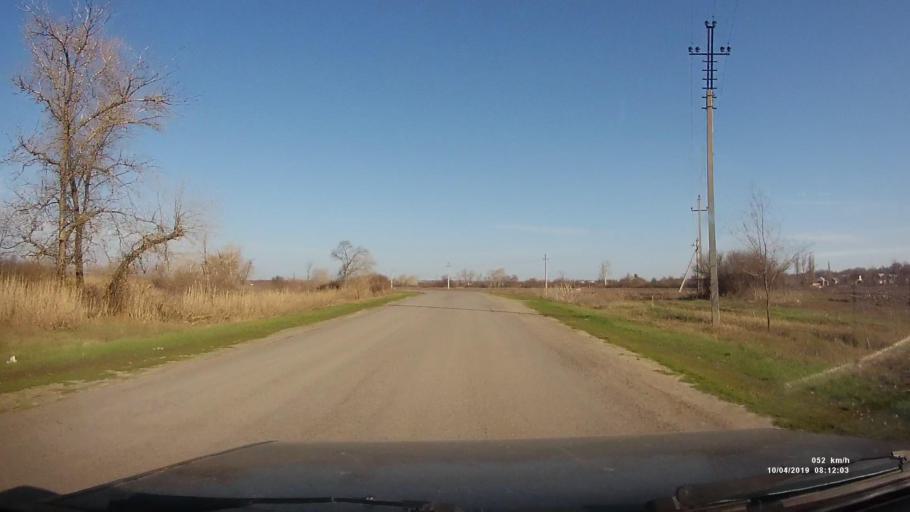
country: RU
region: Rostov
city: Staraya Stanitsa
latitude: 48.3605
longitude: 40.2613
